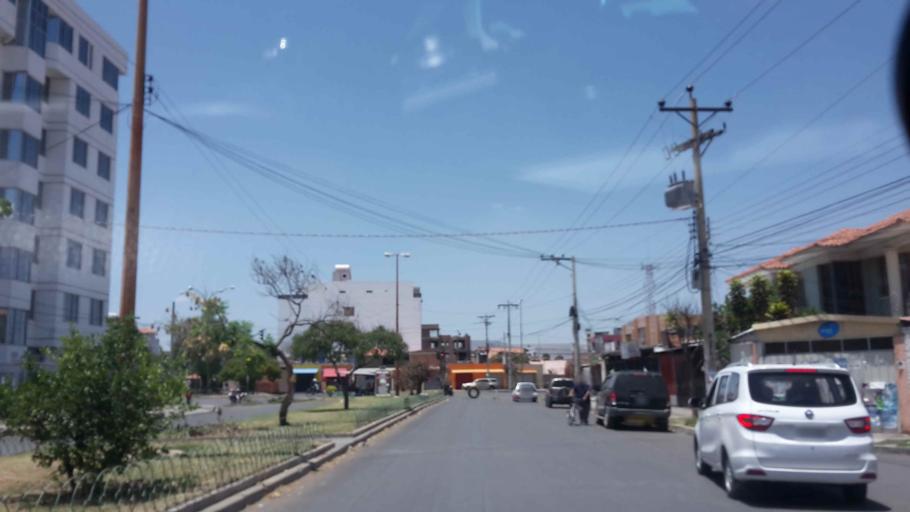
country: BO
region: Cochabamba
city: Cochabamba
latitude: -17.3851
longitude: -66.1858
